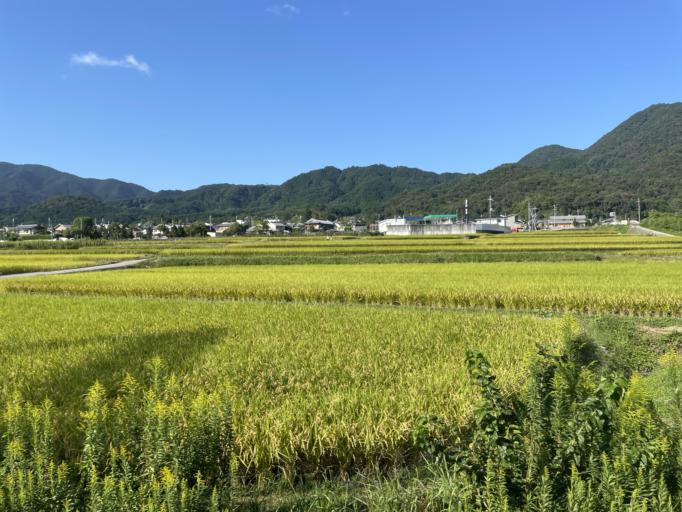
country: JP
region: Nara
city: Gose
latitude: 34.5253
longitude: 135.6993
